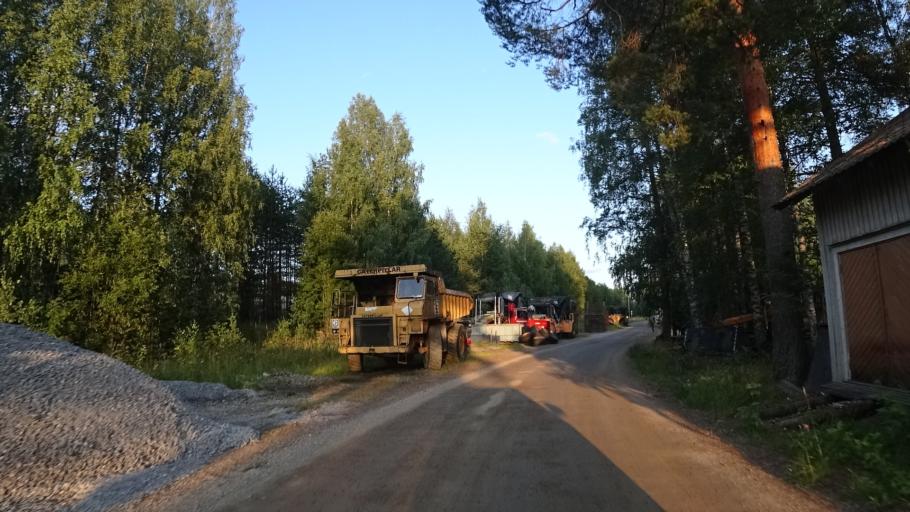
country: FI
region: Southern Savonia
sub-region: Savonlinna
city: Punkaharju
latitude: 61.7605
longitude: 29.3820
